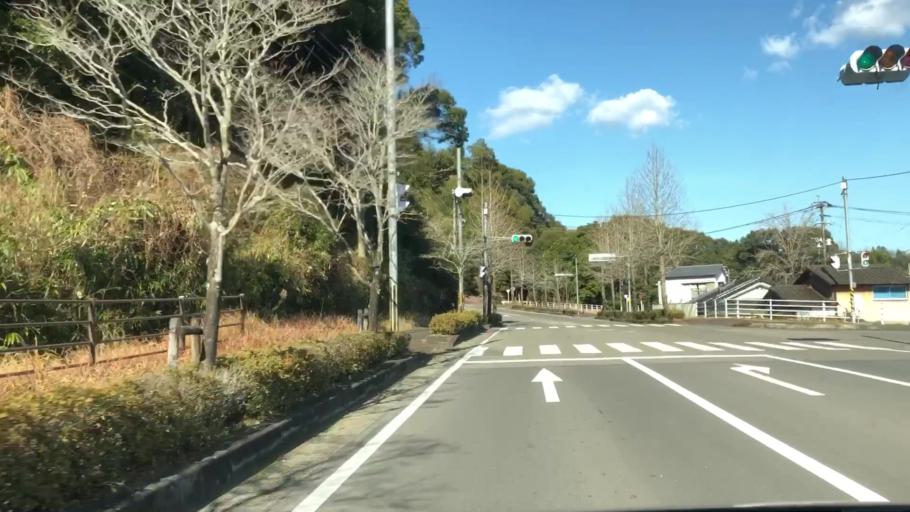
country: JP
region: Kagoshima
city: Satsumasendai
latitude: 31.8268
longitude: 130.4350
